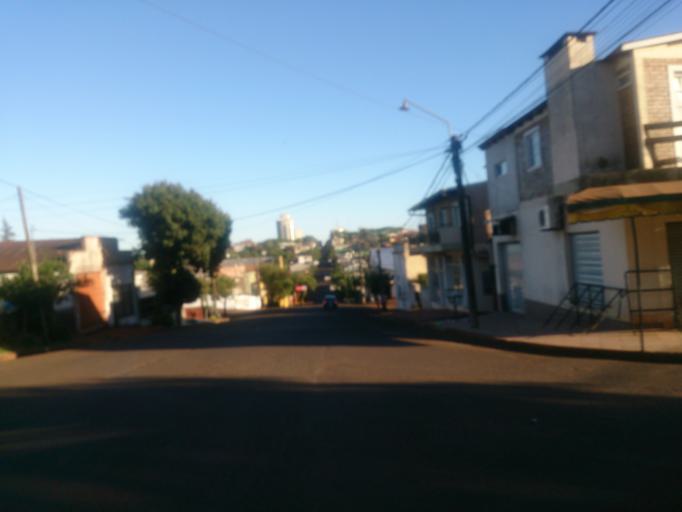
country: AR
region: Misiones
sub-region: Departamento de Obera
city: Obera
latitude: -27.4926
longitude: -55.1193
